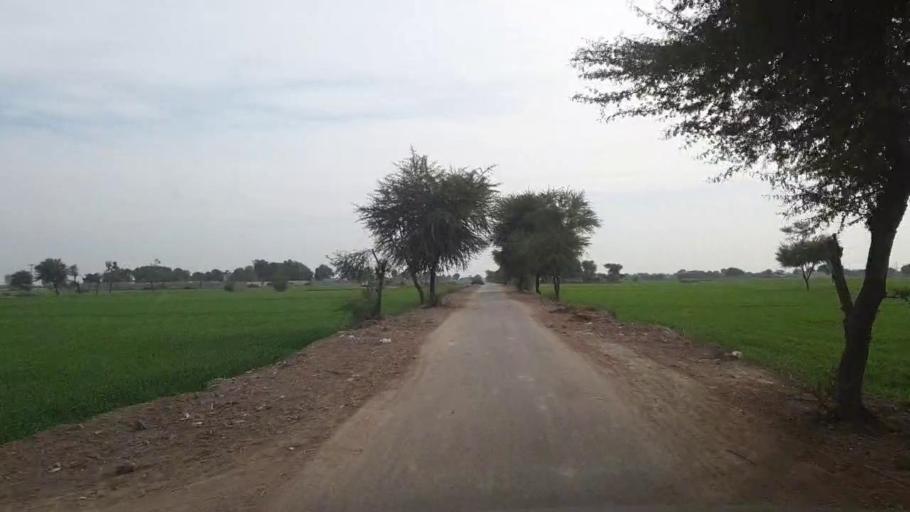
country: PK
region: Sindh
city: Shahpur Chakar
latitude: 26.1067
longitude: 68.5232
